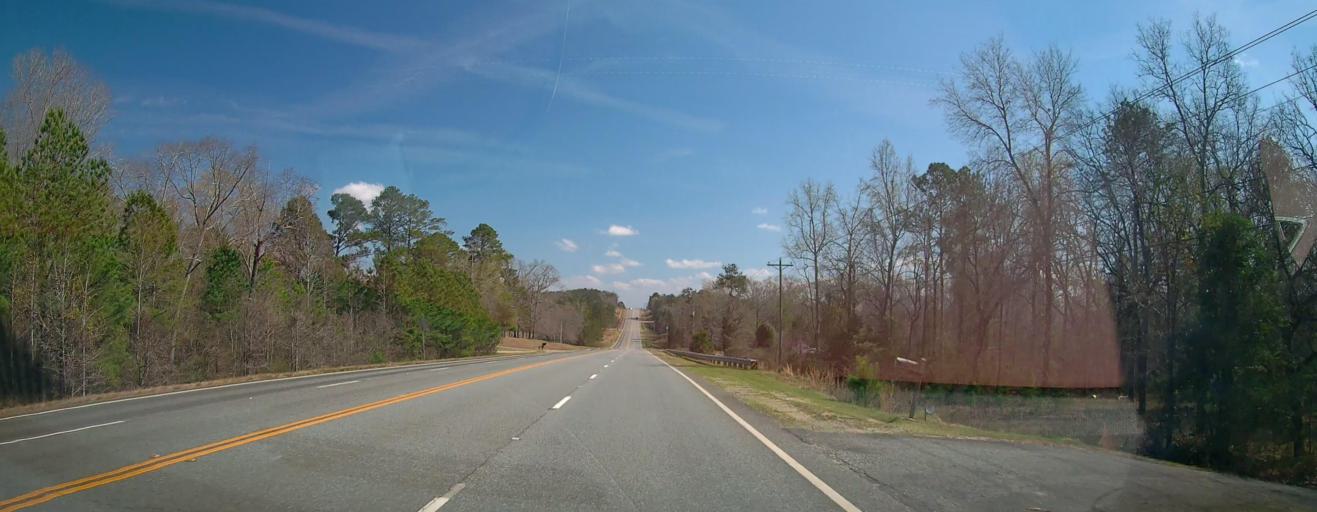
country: US
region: Georgia
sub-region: Wilkinson County
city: Gordon
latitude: 32.9173
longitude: -83.3897
